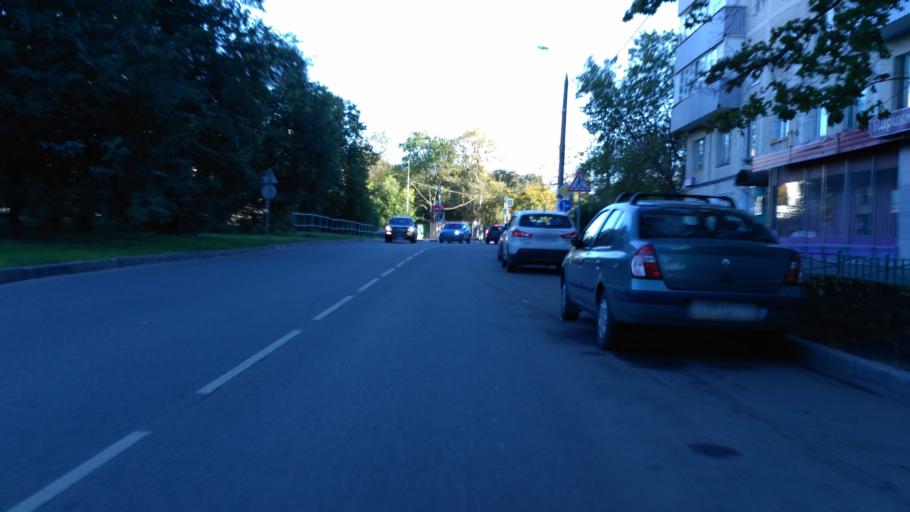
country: RU
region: Moscow
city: Zapadnoye Degunino
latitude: 55.8846
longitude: 37.5328
